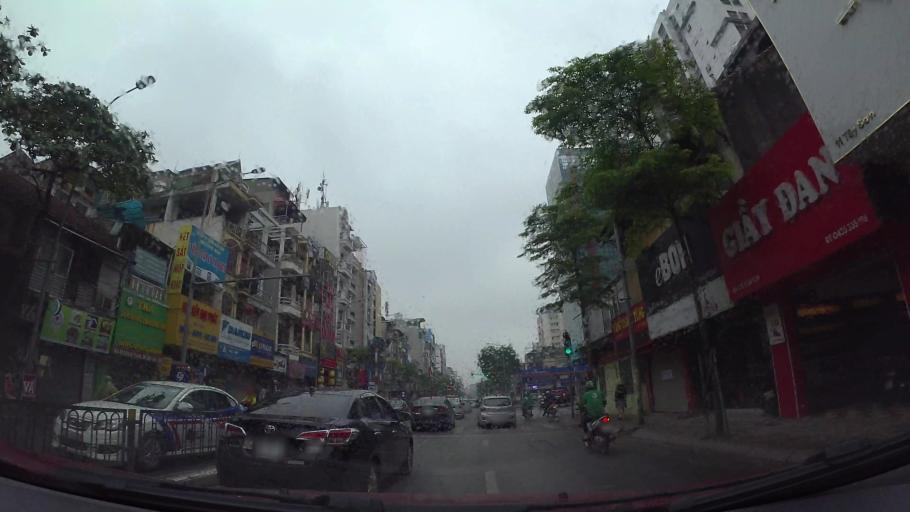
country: VN
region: Ha Noi
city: Dong Da
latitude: 21.0133
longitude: 105.8269
